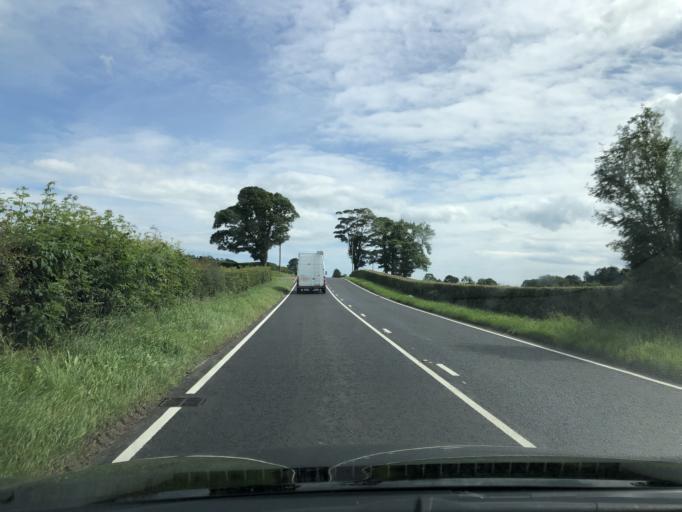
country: GB
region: Northern Ireland
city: Annahilt
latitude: 54.4403
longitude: -5.9410
